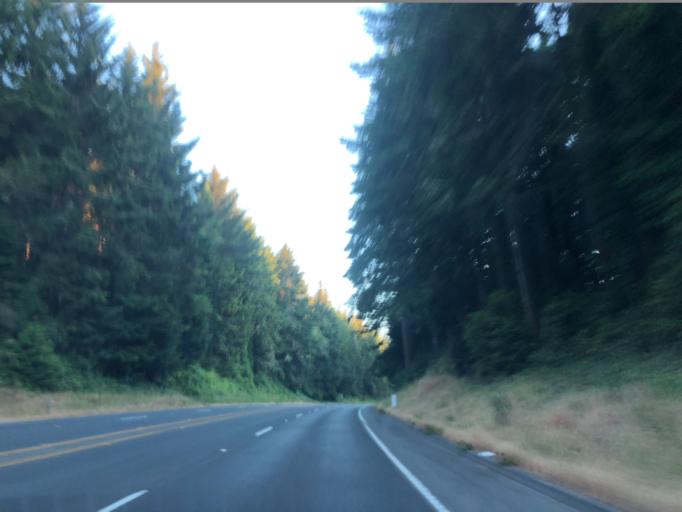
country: US
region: California
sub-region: Humboldt County
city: Westhaven-Moonstone
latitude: 41.1412
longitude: -124.1374
